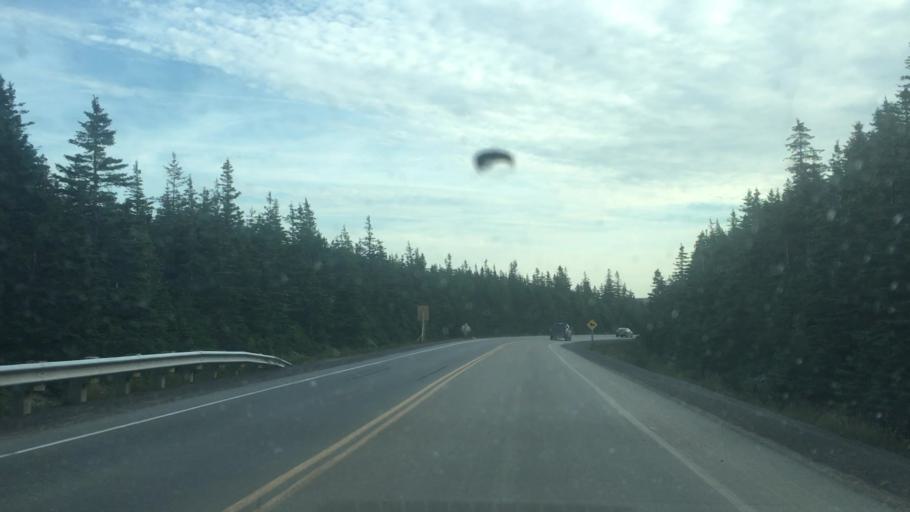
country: CA
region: Nova Scotia
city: Sydney Mines
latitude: 46.8005
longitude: -60.8442
